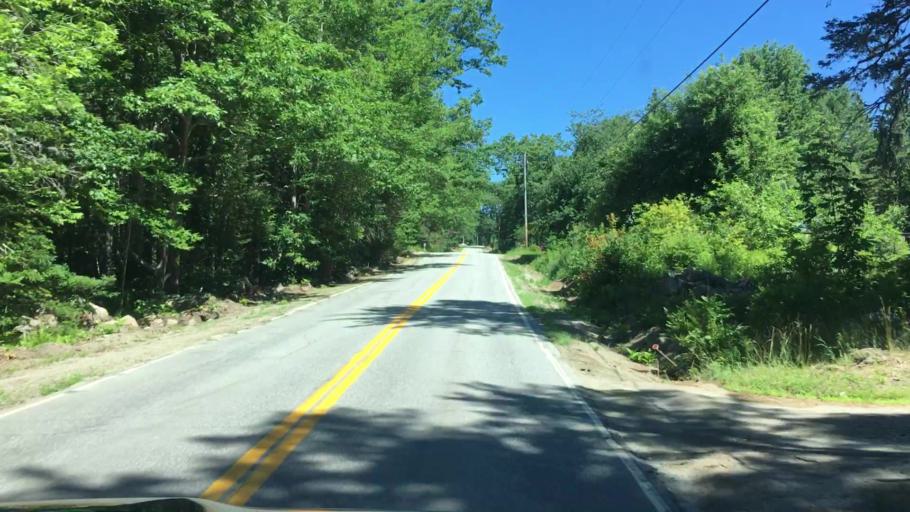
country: US
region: Maine
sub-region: Hancock County
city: Penobscot
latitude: 44.4292
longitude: -68.7134
